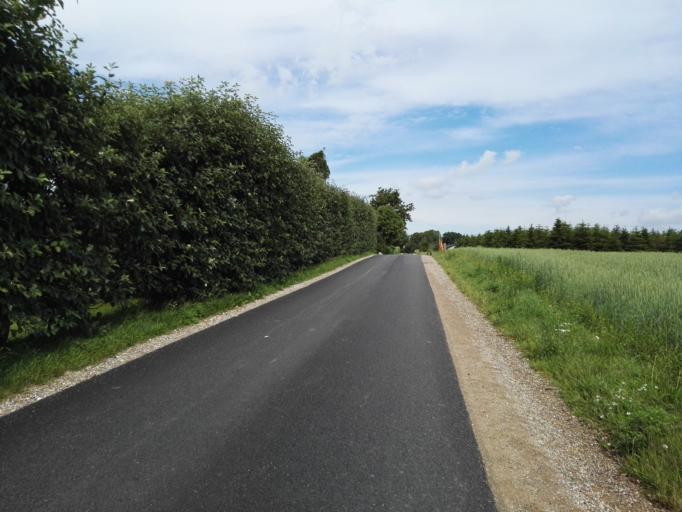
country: DK
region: Capital Region
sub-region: Egedal Kommune
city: Olstykke
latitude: 55.8135
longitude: 12.1765
